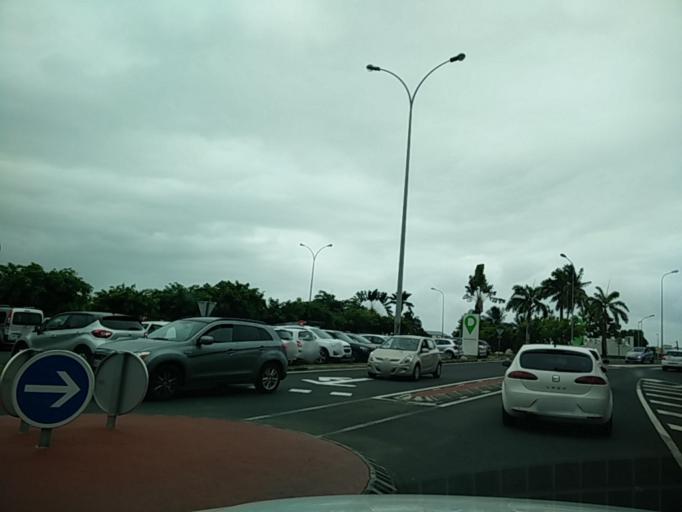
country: GP
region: Guadeloupe
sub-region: Guadeloupe
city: Baie-Mahault
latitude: 16.2540
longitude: -61.5882
